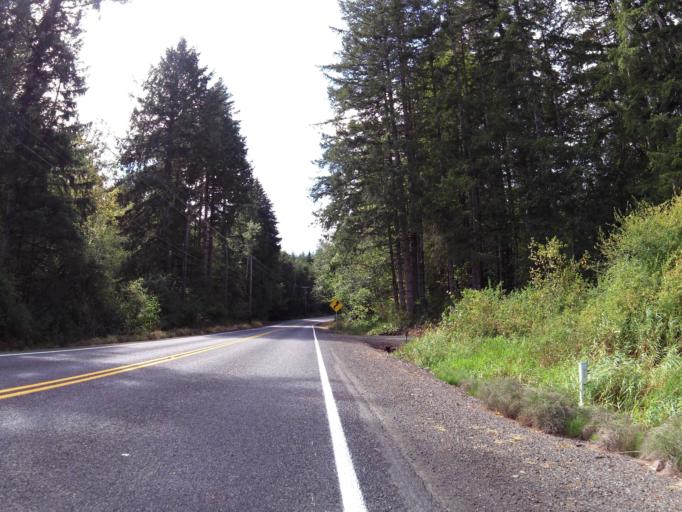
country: US
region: Washington
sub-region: Mason County
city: Shelton
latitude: 47.1508
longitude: -123.0622
